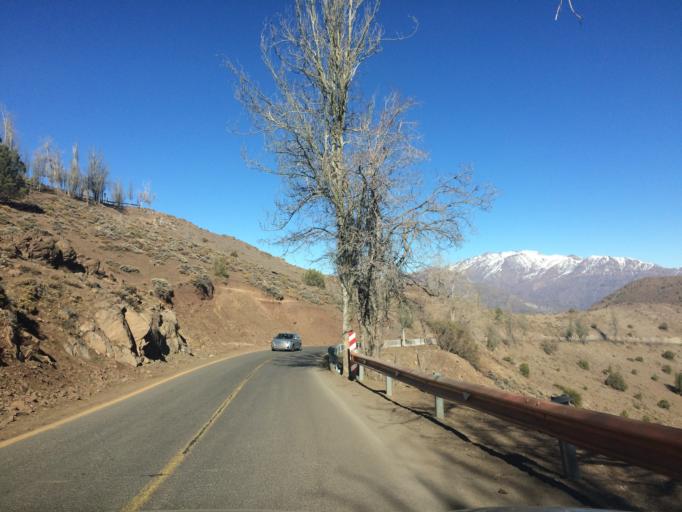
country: CL
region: Santiago Metropolitan
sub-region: Provincia de Santiago
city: Villa Presidente Frei, Nunoa, Santiago, Chile
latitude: -33.3549
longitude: -70.3200
